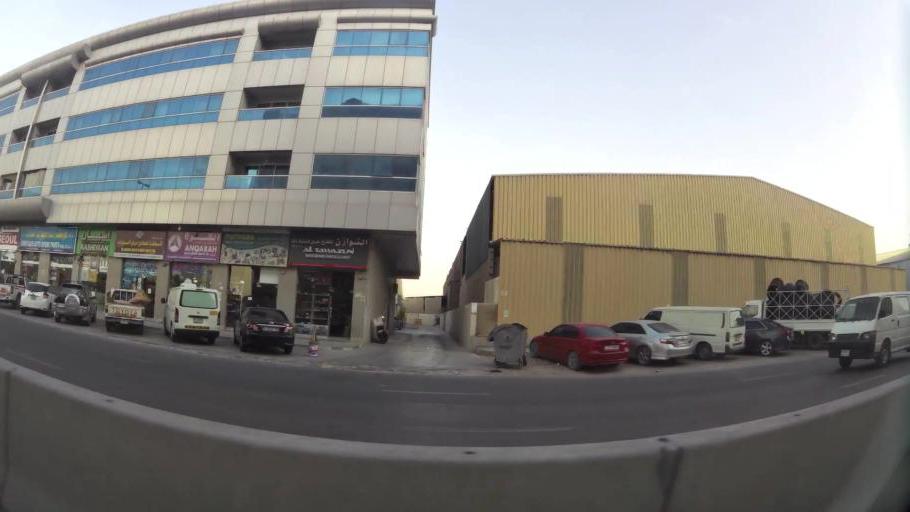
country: AE
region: Ash Shariqah
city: Sharjah
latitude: 25.3155
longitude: 55.3977
